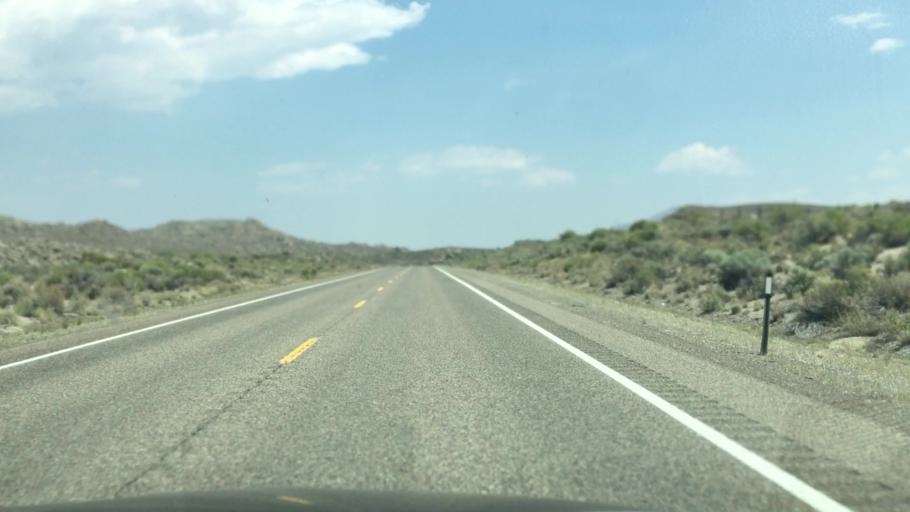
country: US
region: Nevada
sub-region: Elko County
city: Jackpot
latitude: 41.7320
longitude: -114.7917
